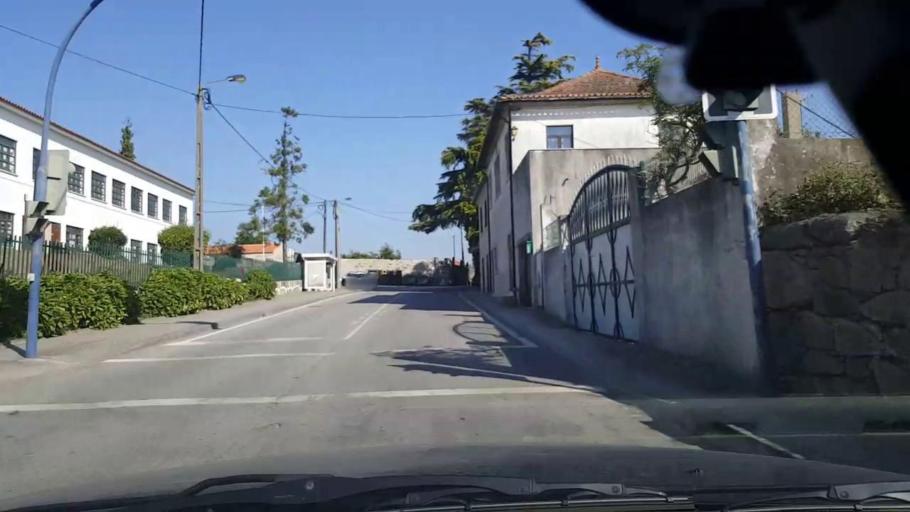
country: PT
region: Porto
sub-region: Vila do Conde
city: Arvore
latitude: 41.3073
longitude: -8.6790
